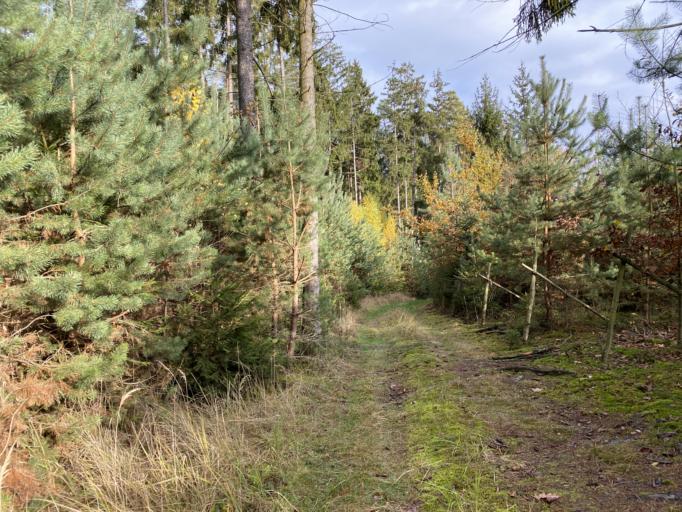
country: DE
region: Bavaria
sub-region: Upper Bavaria
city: Wolfersdorf
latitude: 48.5017
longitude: 11.7194
